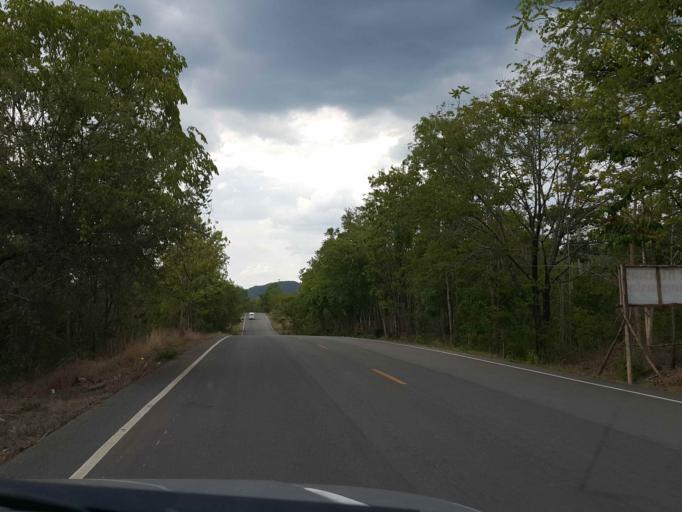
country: TH
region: Sukhothai
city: Thung Saliam
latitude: 17.3592
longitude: 99.4129
